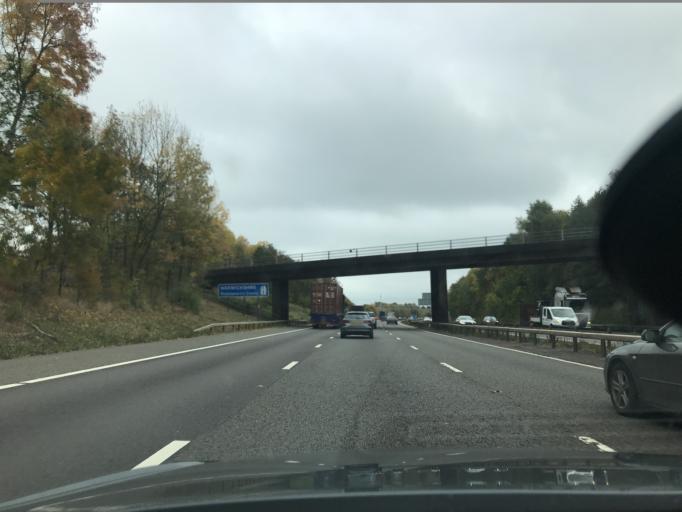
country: GB
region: England
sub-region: Solihull
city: Cheswick Green
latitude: 52.3453
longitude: -1.7958
